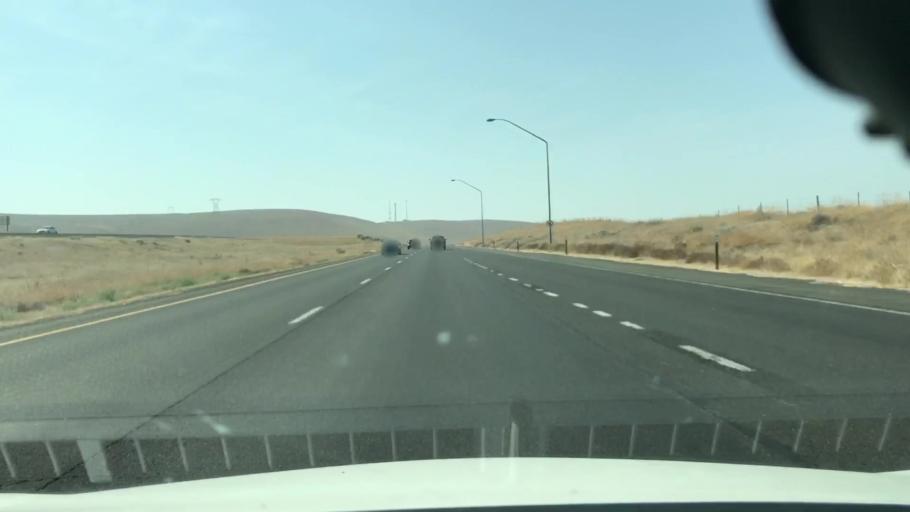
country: US
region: Washington
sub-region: Grant County
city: Quincy
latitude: 47.0171
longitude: -119.9487
